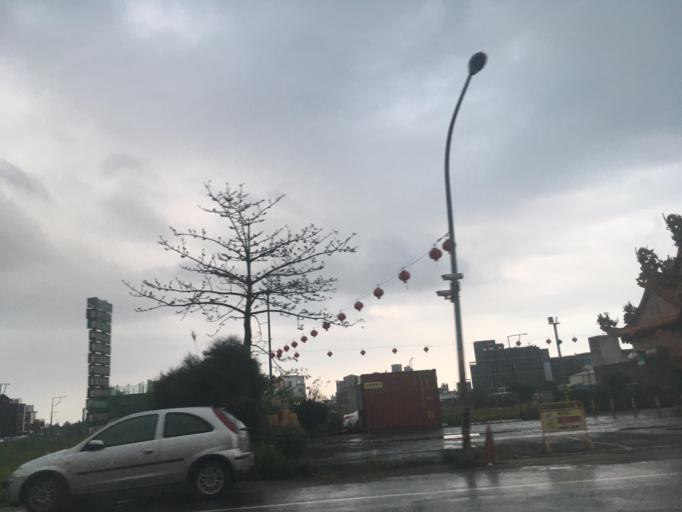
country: TW
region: Taiwan
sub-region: Yilan
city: Yilan
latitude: 24.8609
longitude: 121.8275
